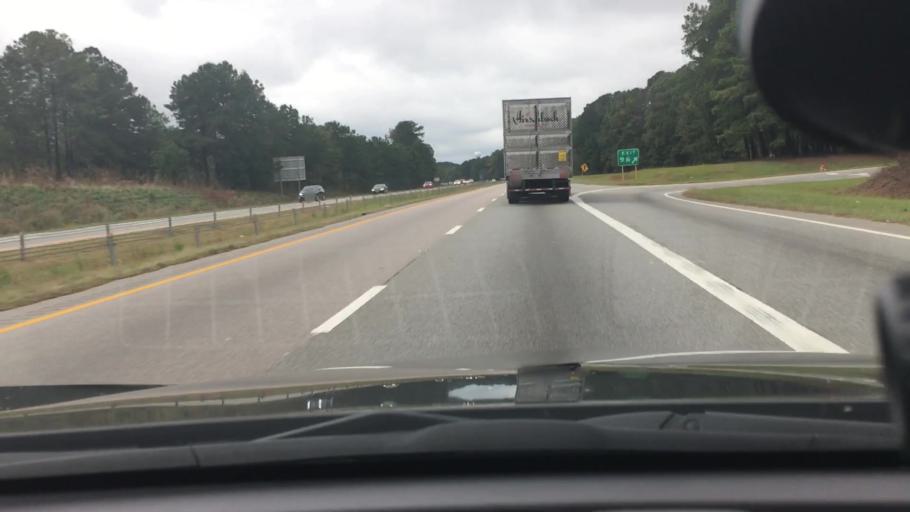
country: US
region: North Carolina
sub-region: Wake County
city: Apex
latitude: 35.7234
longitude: -78.8245
